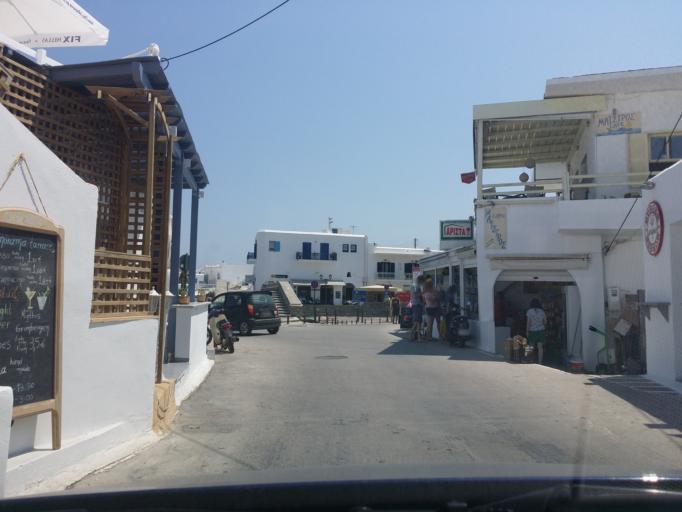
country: GR
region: South Aegean
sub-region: Nomos Kykladon
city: Naousa
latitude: 37.1239
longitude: 25.2364
